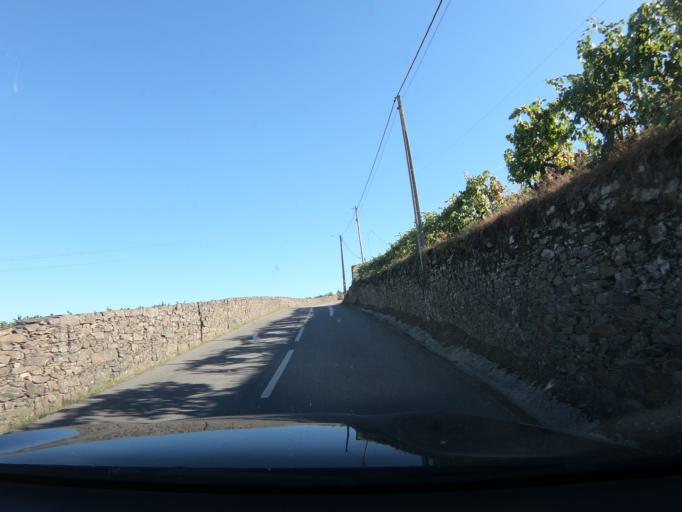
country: PT
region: Vila Real
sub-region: Sabrosa
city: Vilela
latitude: 41.2267
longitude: -7.5640
